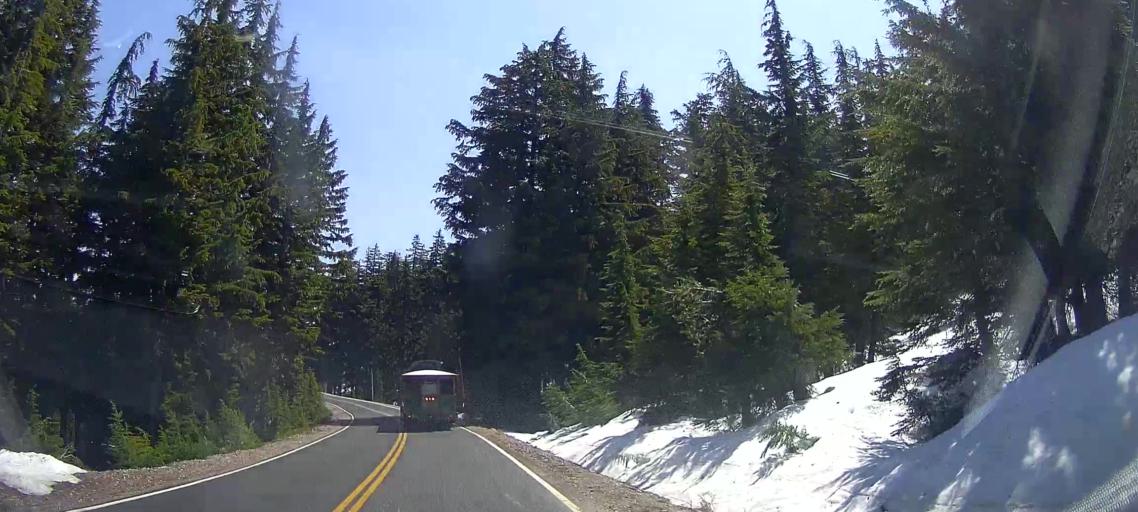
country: US
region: Oregon
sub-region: Jackson County
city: Shady Cove
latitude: 42.9803
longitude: -122.1268
